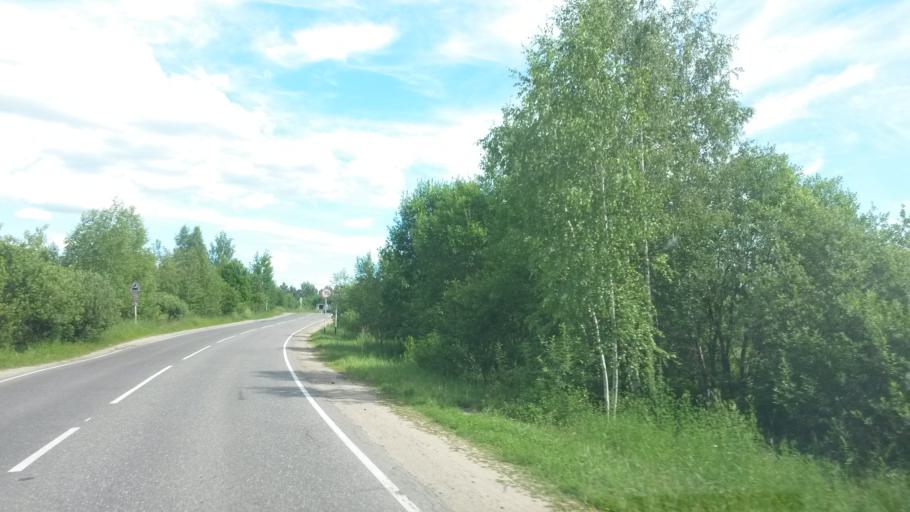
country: RU
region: Ivanovo
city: Zavolzhsk
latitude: 57.5033
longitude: 42.1092
